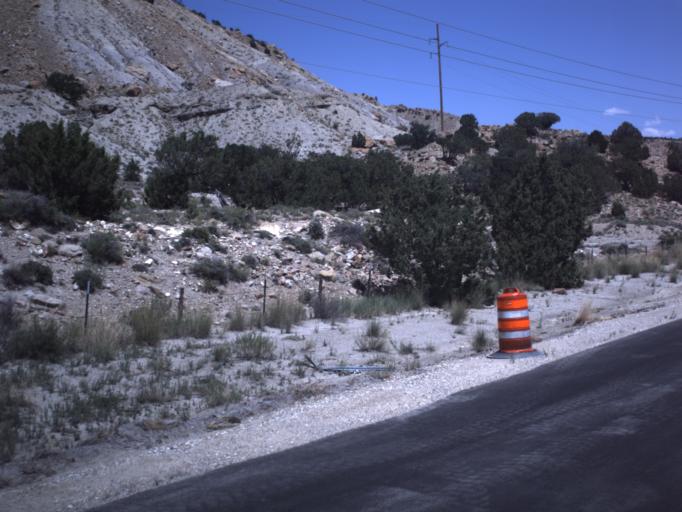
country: US
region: Utah
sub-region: Emery County
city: Orangeville
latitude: 39.2747
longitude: -111.1653
